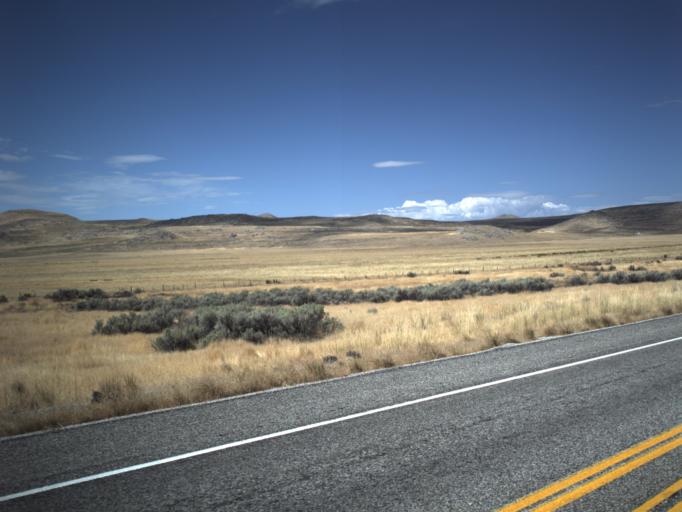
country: US
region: Utah
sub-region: Box Elder County
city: Tremonton
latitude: 41.6415
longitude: -112.4282
